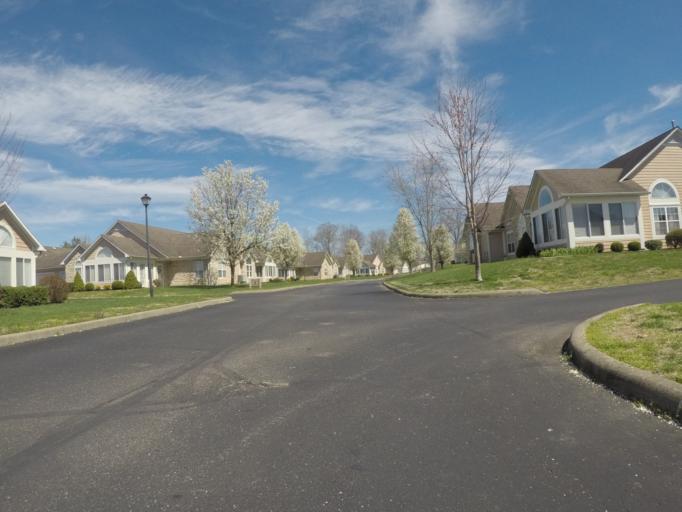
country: US
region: West Virginia
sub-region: Cabell County
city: Pea Ridge
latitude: 38.4085
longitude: -82.3123
